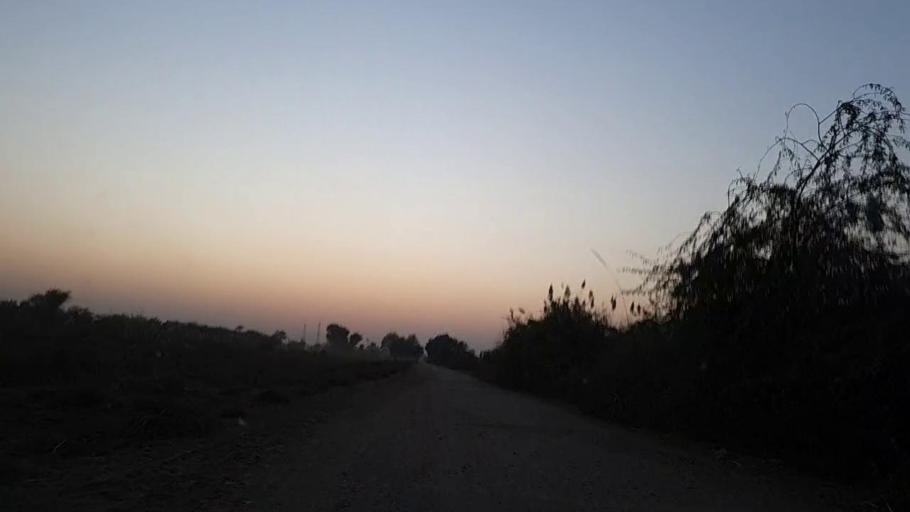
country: PK
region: Sindh
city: Hala
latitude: 25.9600
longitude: 68.3921
